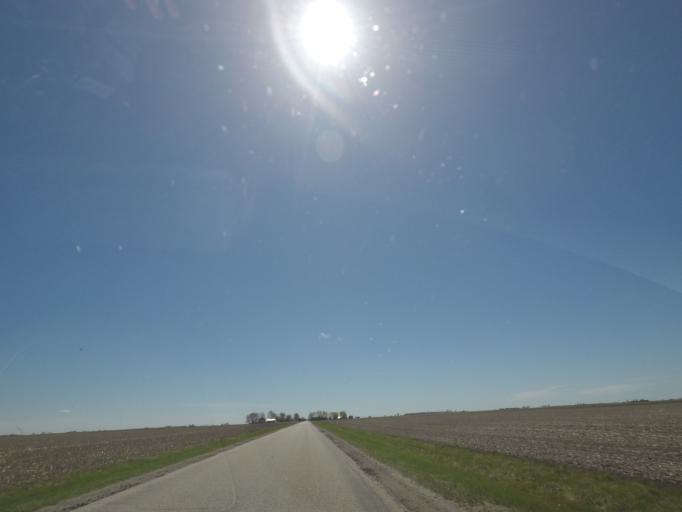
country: US
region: Illinois
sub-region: Logan County
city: Atlanta
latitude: 40.1891
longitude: -89.1941
